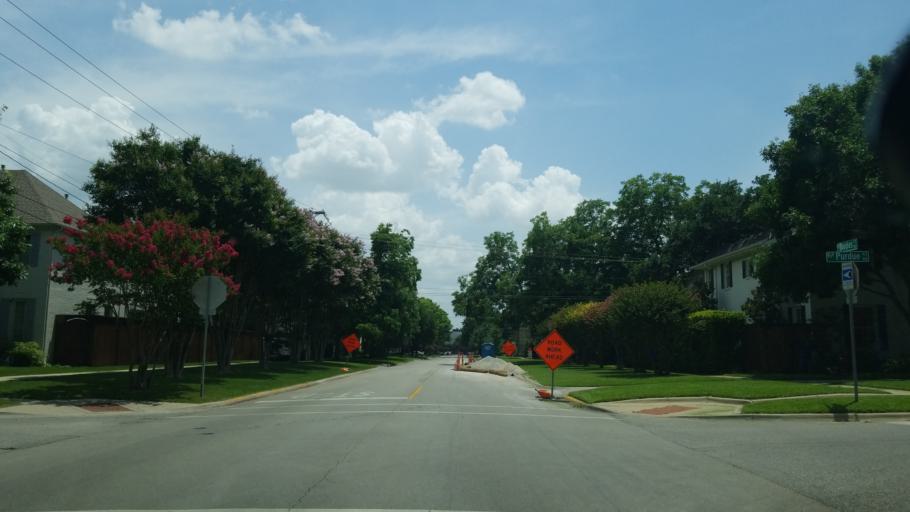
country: US
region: Texas
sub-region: Dallas County
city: University Park
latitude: 32.8541
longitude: -96.8087
